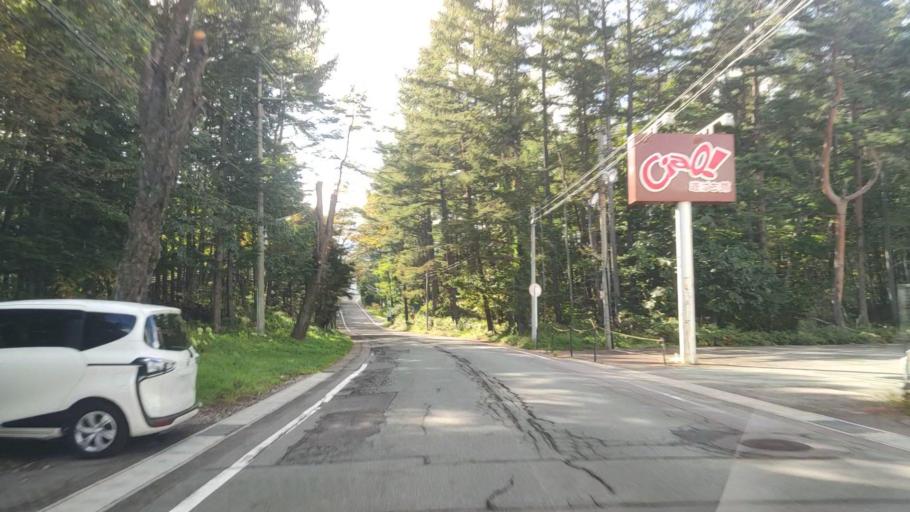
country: JP
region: Gunma
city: Nakanojomachi
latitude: 36.6221
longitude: 138.6123
